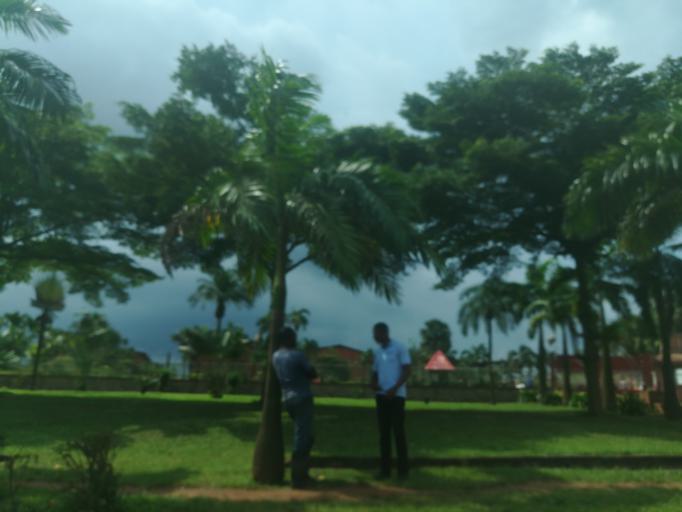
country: NG
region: Lagos
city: Ikorodu
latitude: 6.6402
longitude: 3.5480
